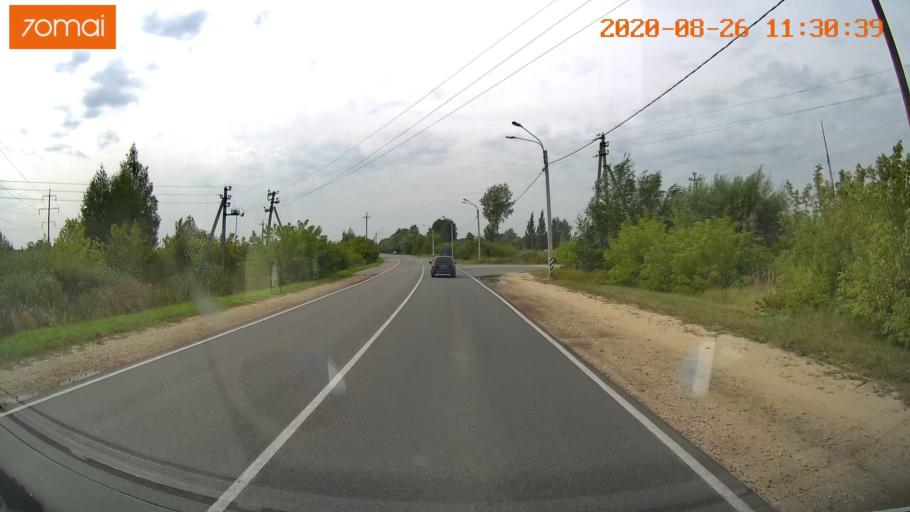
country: RU
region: Rjazan
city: Shilovo
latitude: 54.3141
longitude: 40.8804
